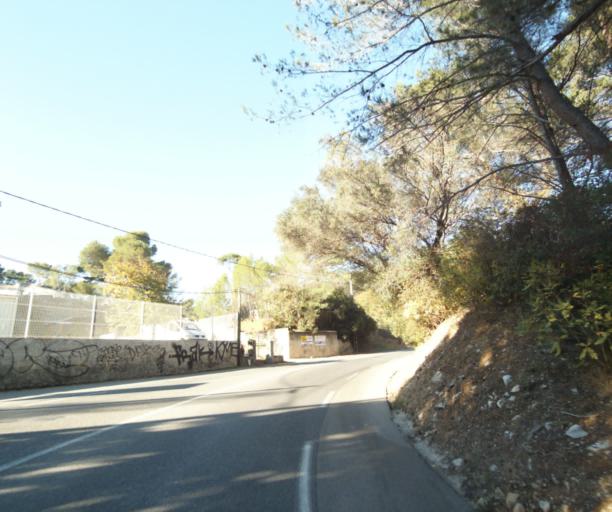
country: FR
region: Provence-Alpes-Cote d'Azur
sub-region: Departement des Bouches-du-Rhone
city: La Ciotat
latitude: 43.1973
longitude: 5.5925
